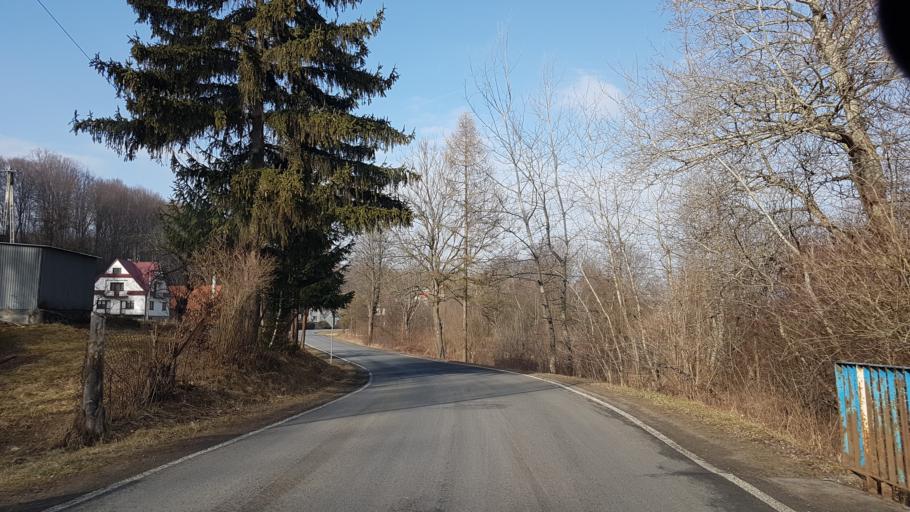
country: PL
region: Lesser Poland Voivodeship
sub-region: Powiat limanowski
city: Lukowica
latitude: 49.6328
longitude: 20.5063
